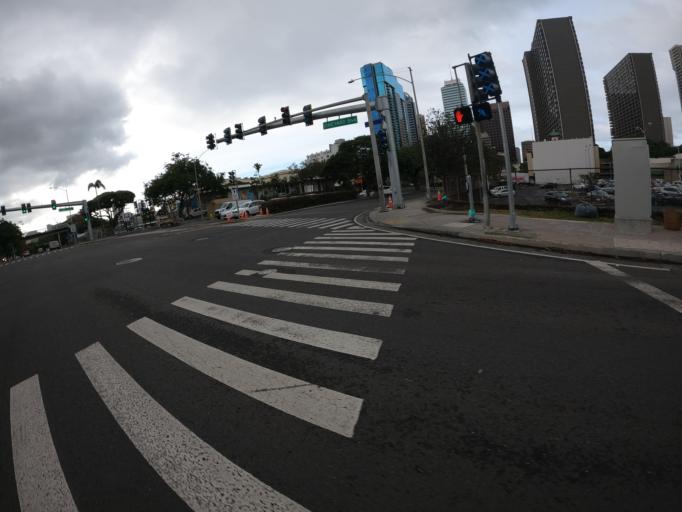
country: US
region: Hawaii
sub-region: Honolulu County
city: Honolulu
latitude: 21.3130
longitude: -157.8567
